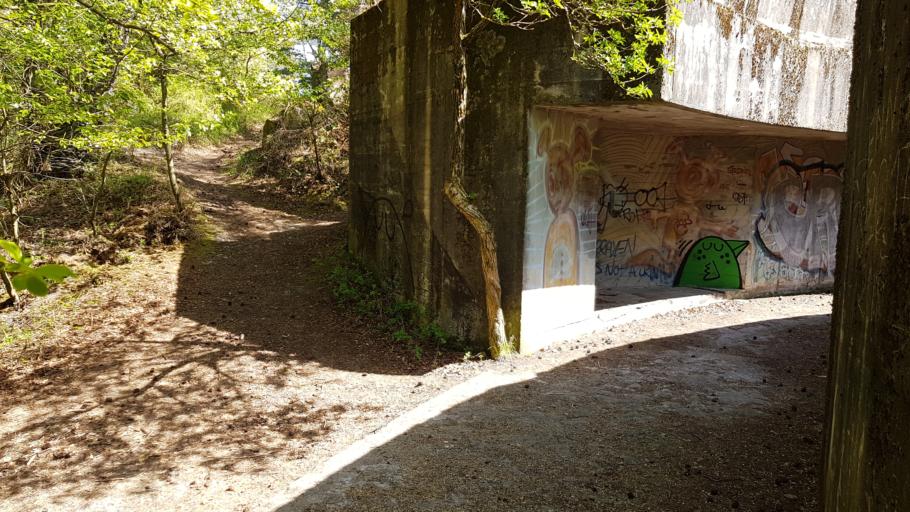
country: DK
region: Capital Region
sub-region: Bornholm Kommune
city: Nexo
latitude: 55.0010
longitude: 15.0808
